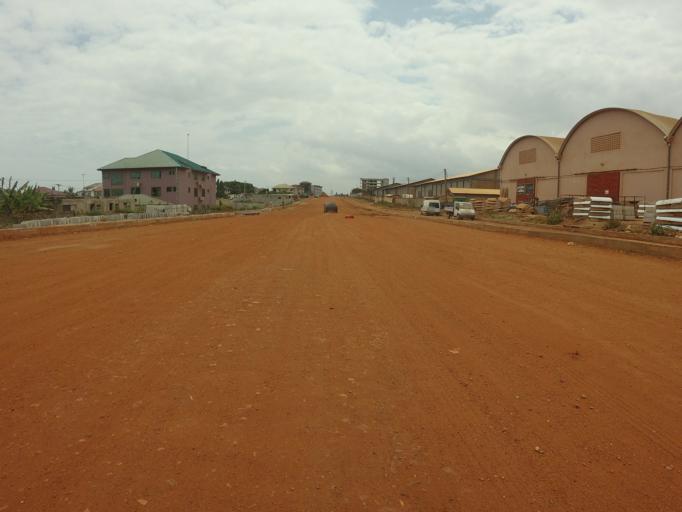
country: GH
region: Greater Accra
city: Medina Estates
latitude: 5.6269
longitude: -0.1482
